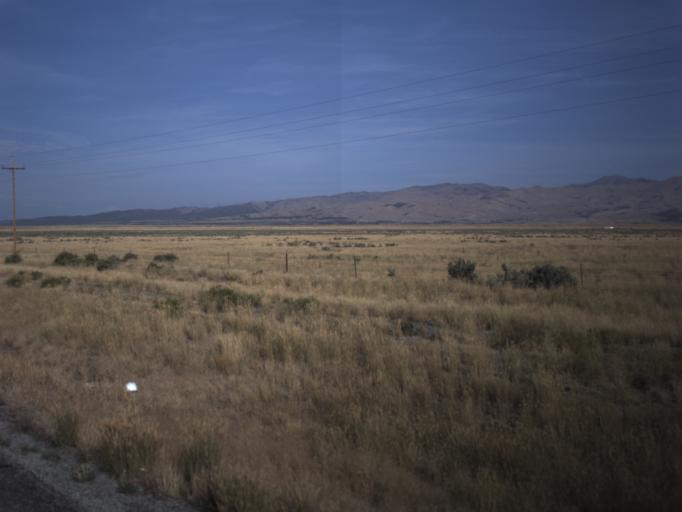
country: US
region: Idaho
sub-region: Oneida County
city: Malad City
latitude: 41.9661
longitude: -112.9676
